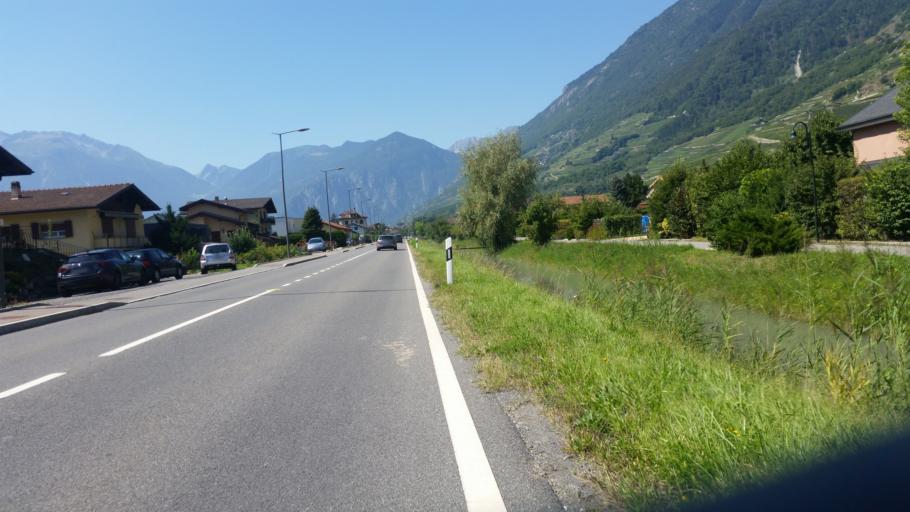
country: CH
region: Valais
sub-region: Martigny District
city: Fully
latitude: 46.1475
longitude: 7.1340
